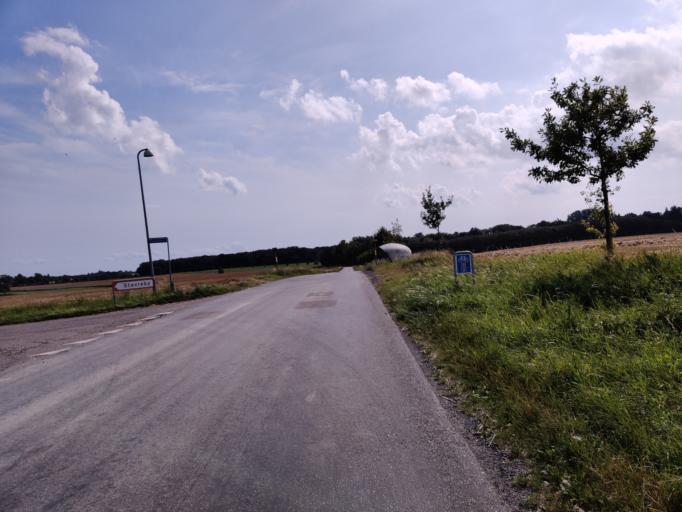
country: DK
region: Zealand
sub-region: Guldborgsund Kommune
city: Nykobing Falster
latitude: 54.6524
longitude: 11.8876
